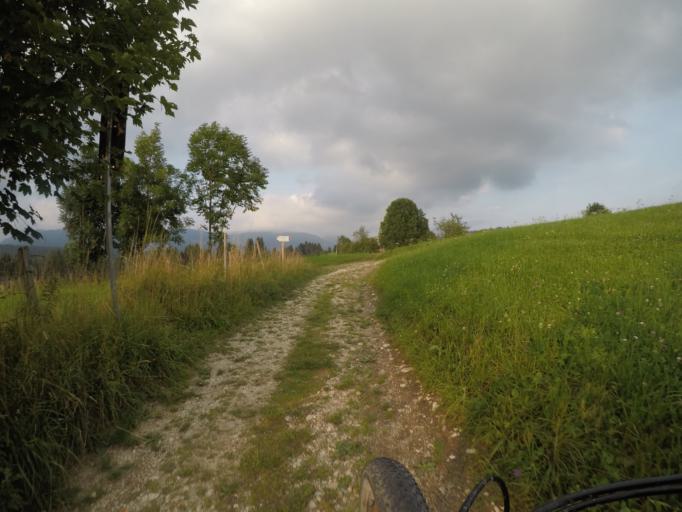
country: IT
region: Veneto
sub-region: Provincia di Vicenza
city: Gallio
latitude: 45.8769
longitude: 11.5290
